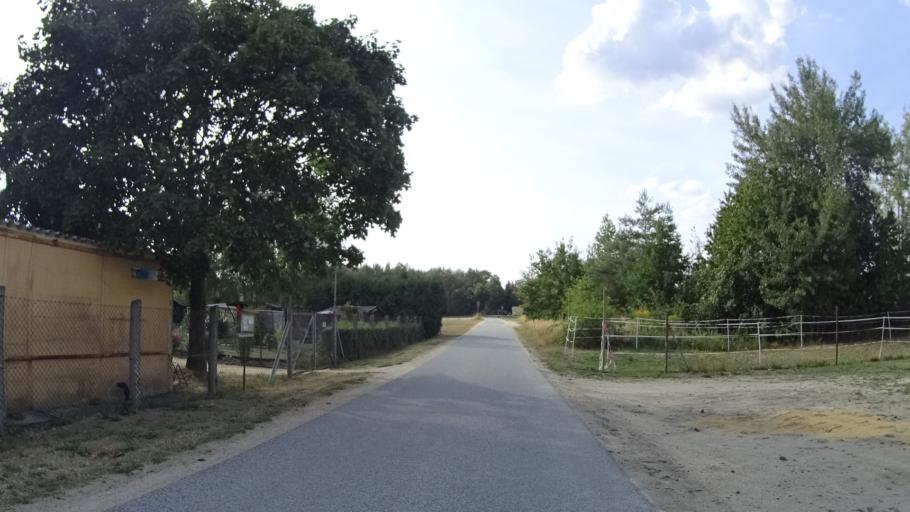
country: DE
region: Saxony
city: Ostritz
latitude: 51.0737
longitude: 14.9663
